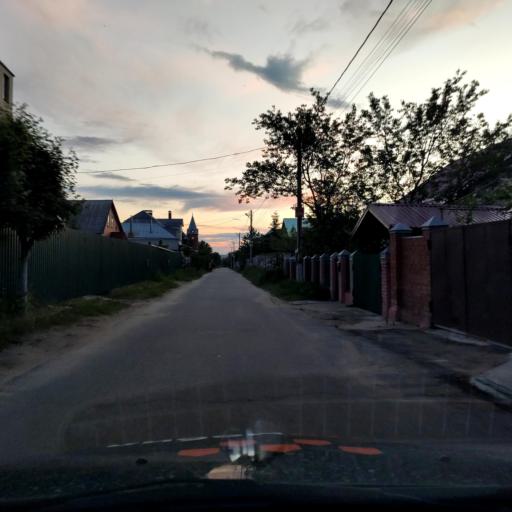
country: RU
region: Voronezj
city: Podgornoye
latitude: 51.7465
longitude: 39.1596
